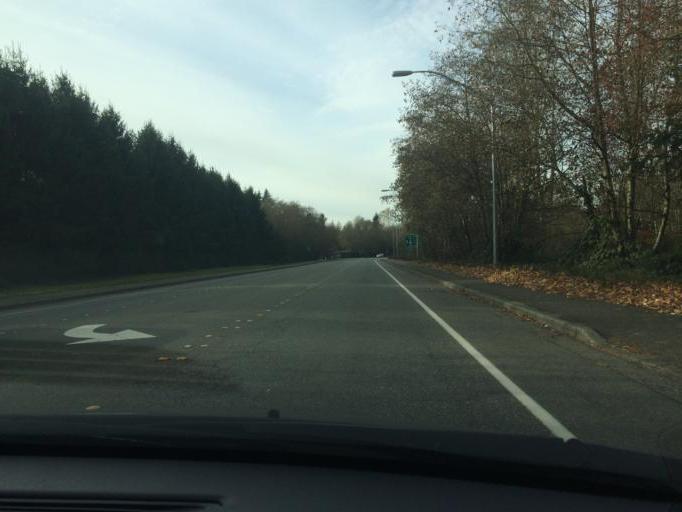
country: US
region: Washington
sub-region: Whatcom County
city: Bellingham
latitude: 48.7147
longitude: -122.4834
